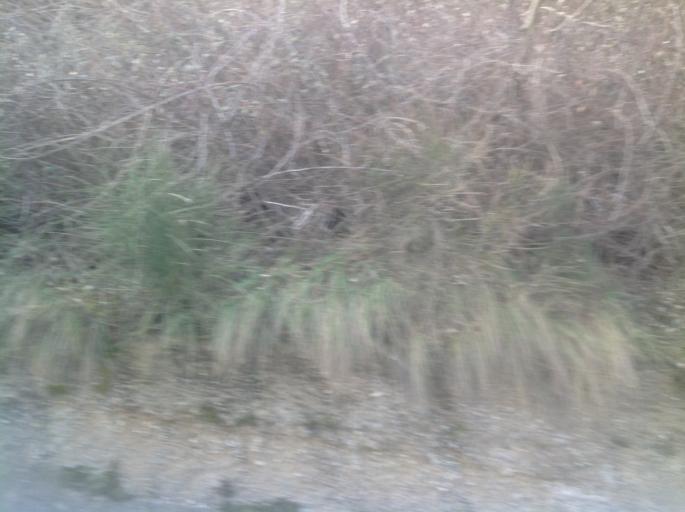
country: IT
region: Calabria
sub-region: Provincia di Cosenza
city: Civita
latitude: 39.8505
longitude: 16.3076
